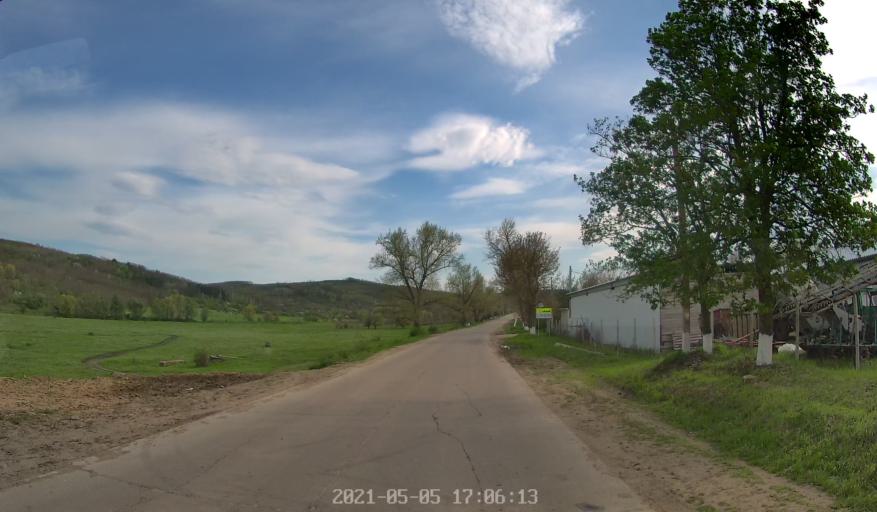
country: MD
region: Chisinau
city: Vadul lui Voda
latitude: 47.0223
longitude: 29.1402
